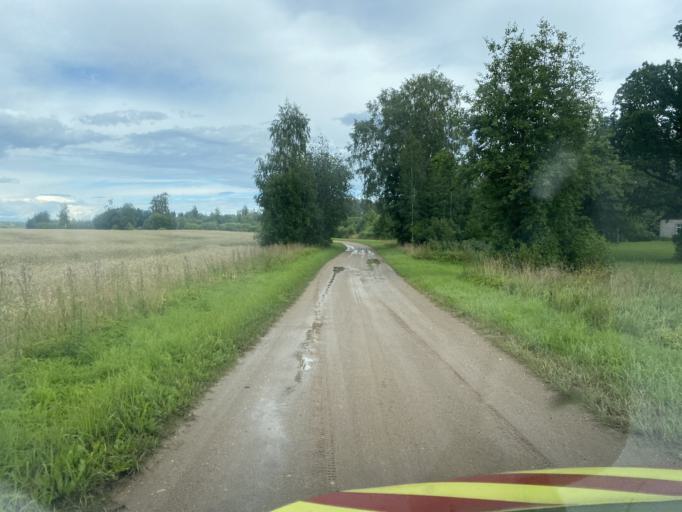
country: EE
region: Valgamaa
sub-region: Torva linn
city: Torva
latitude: 58.0966
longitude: 26.0003
